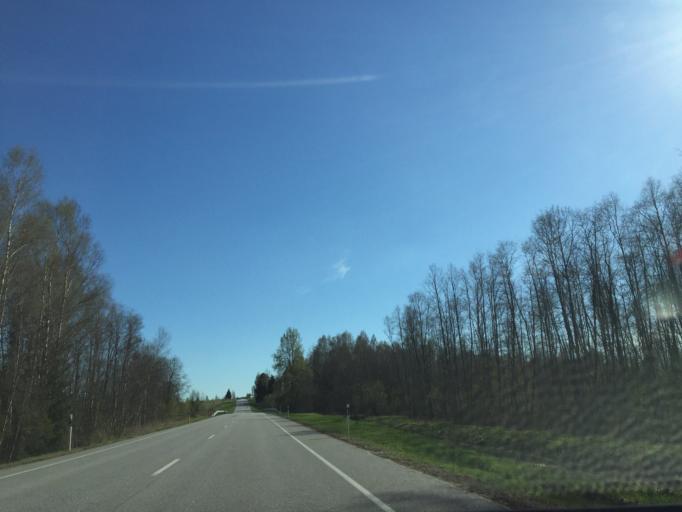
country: EE
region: Vorumaa
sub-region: Antsla vald
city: Vana-Antsla
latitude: 57.8896
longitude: 26.2873
